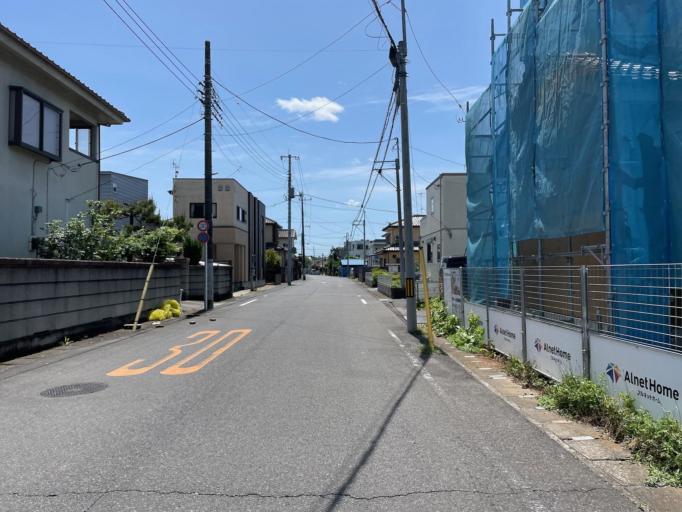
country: JP
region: Tochigi
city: Sano
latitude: 36.3249
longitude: 139.5864
